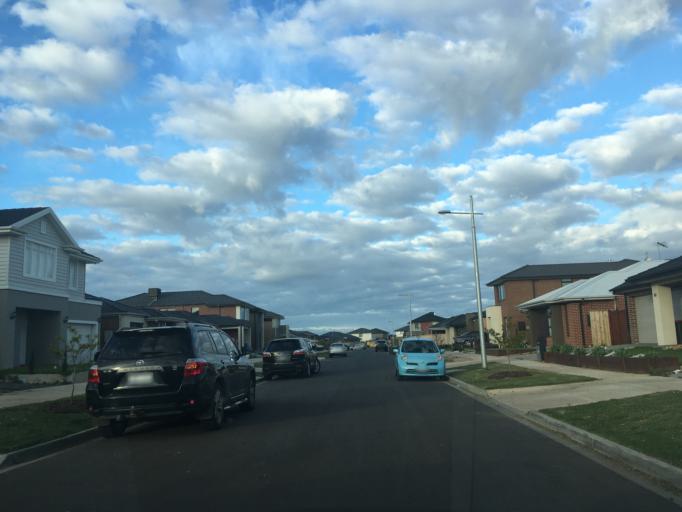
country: AU
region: Victoria
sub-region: Wyndham
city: Hoppers Crossing
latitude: -37.8865
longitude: 144.7103
